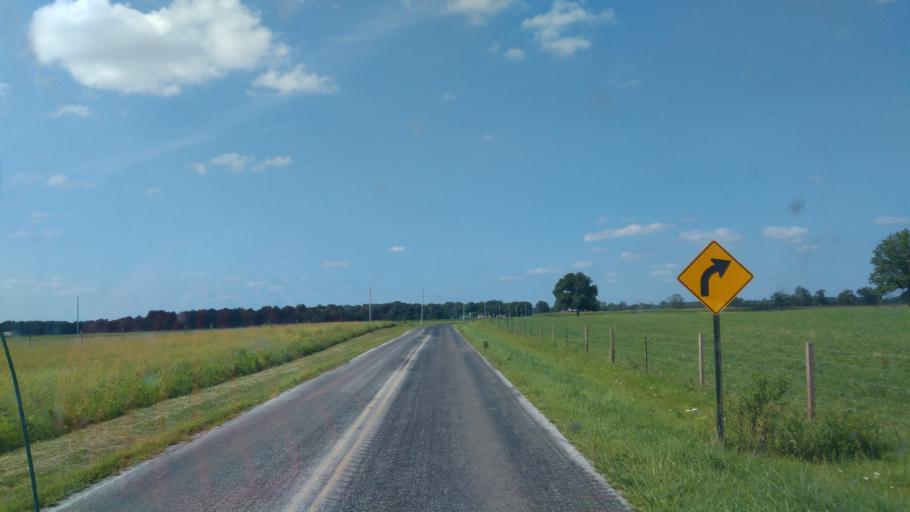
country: US
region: Ohio
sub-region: Hardin County
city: Kenton
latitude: 40.5996
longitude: -83.4657
